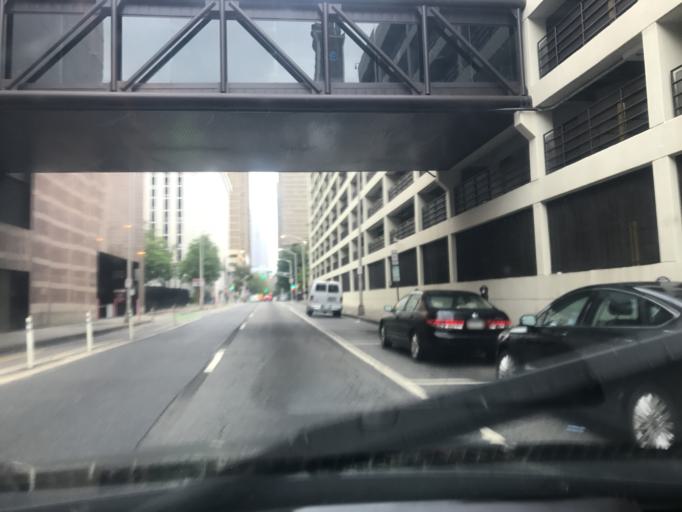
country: US
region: Georgia
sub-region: Fulton County
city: Atlanta
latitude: 33.7572
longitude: -84.3861
